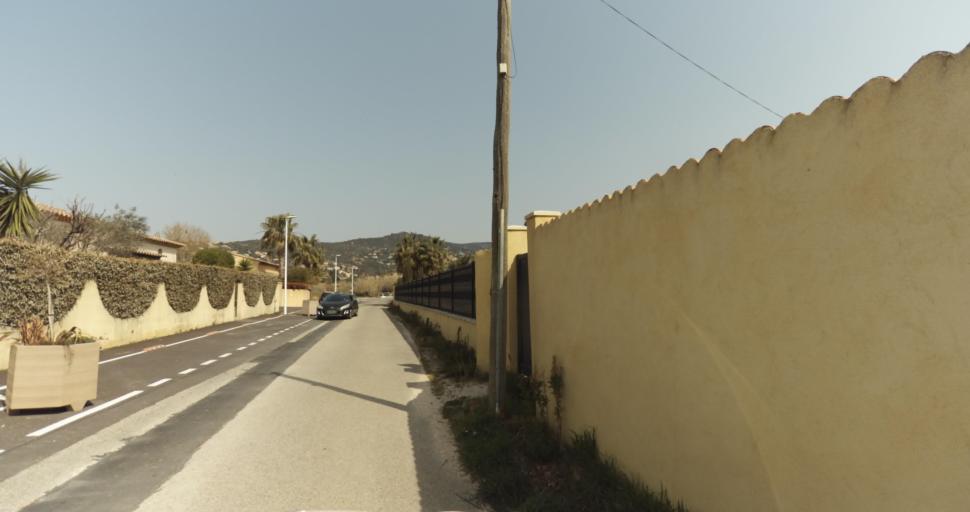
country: FR
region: Provence-Alpes-Cote d'Azur
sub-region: Departement du Var
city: Bormes-les-Mimosas
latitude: 43.1358
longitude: 6.3362
